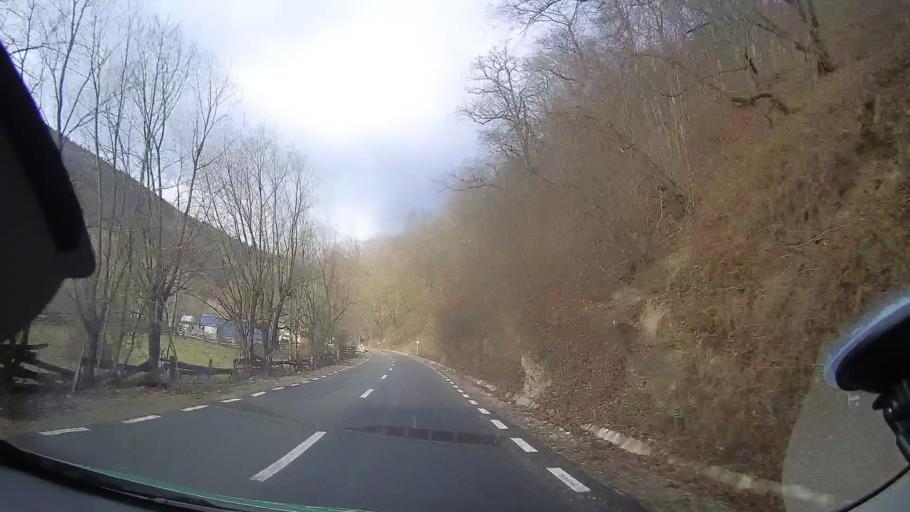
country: RO
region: Cluj
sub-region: Comuna Valea Ierii
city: Valea Ierii
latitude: 46.6412
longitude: 23.3577
